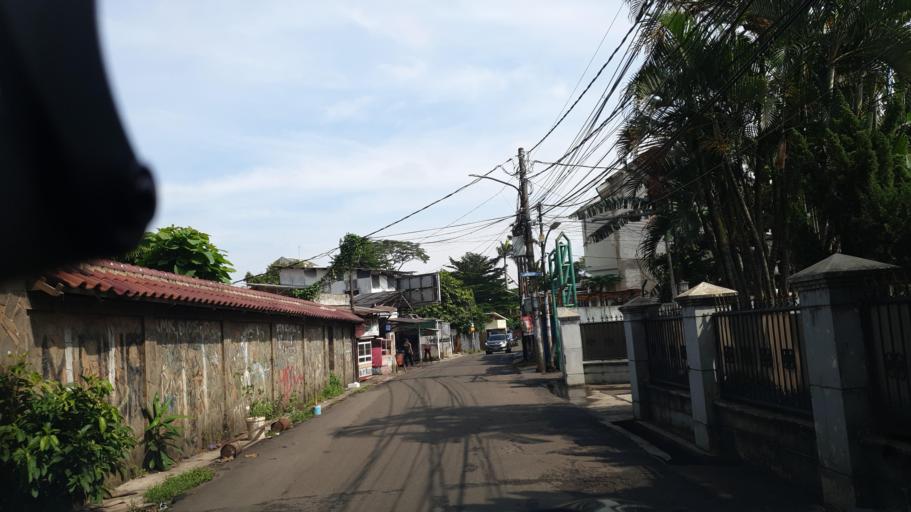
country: ID
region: West Java
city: Pamulang
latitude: -6.3084
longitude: 106.7662
